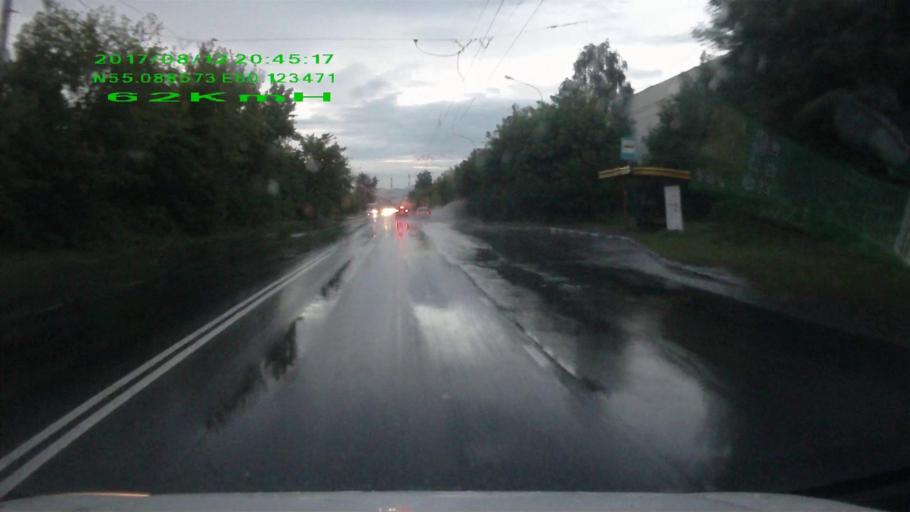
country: RU
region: Chelyabinsk
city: Miass
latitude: 55.0887
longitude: 60.1236
